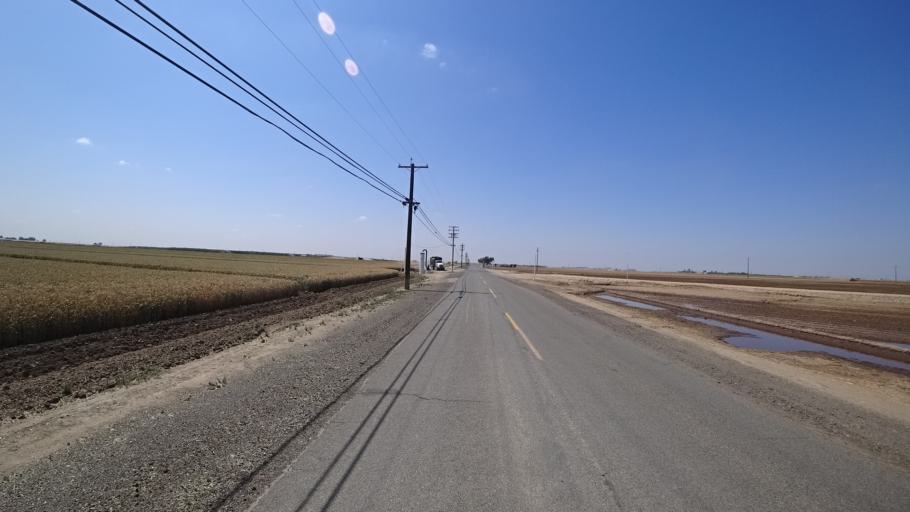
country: US
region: California
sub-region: Kings County
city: Home Garden
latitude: 36.2637
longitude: -119.6189
